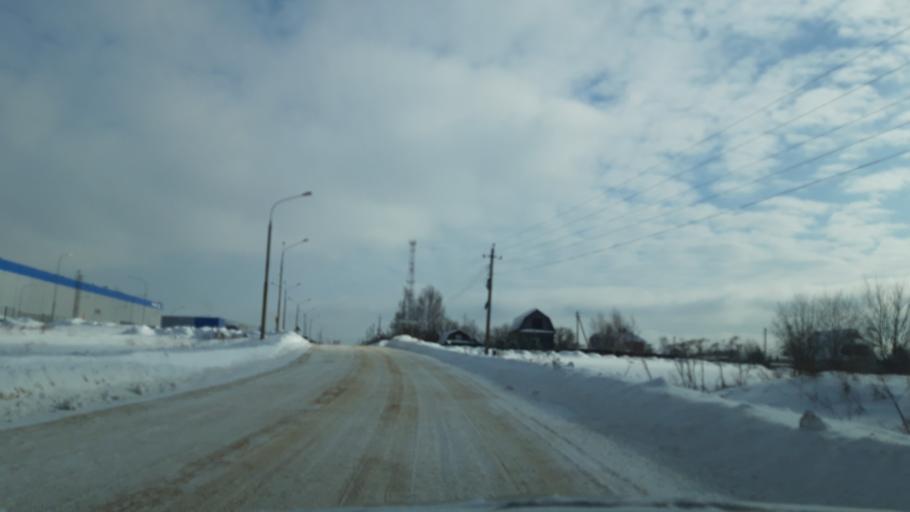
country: RU
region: Moskovskaya
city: Yermolino
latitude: 56.1449
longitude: 37.3733
